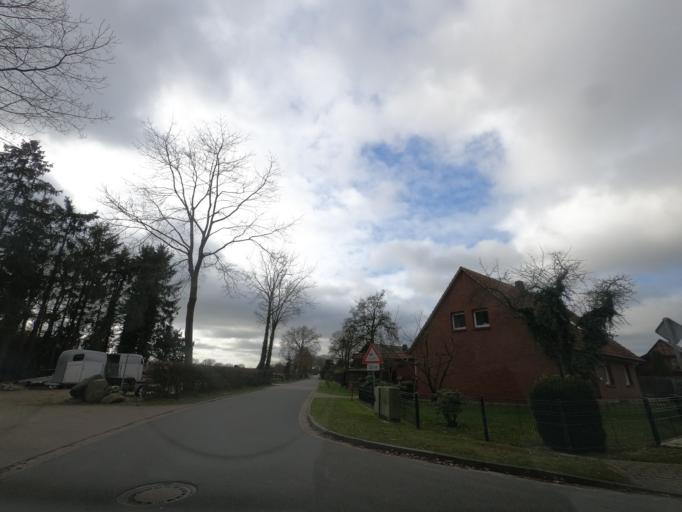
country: DE
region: Lower Saxony
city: Herzlake
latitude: 52.6879
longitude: 7.5959
